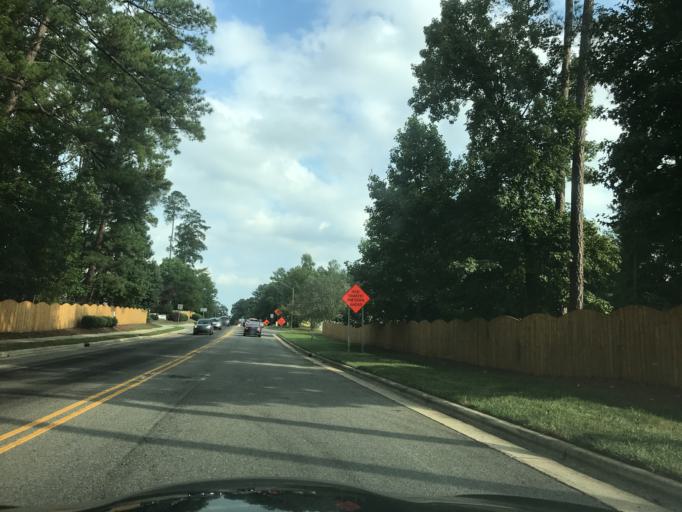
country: US
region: North Carolina
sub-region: Durham County
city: Durham
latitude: 35.9039
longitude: -78.9309
